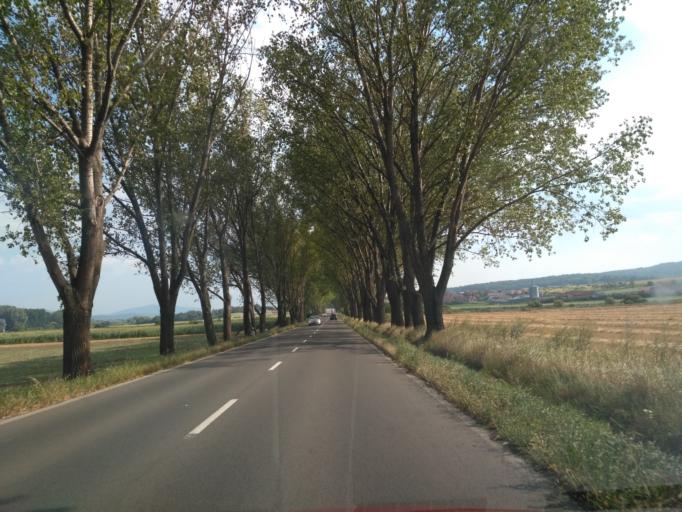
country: SK
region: Kosicky
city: Kosice
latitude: 48.8124
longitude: 21.3003
